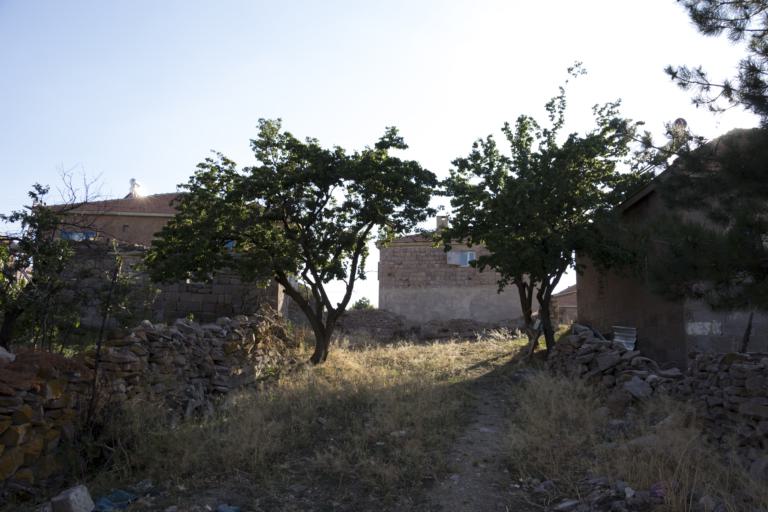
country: TR
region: Kayseri
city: Toklar
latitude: 38.4220
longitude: 36.0944
